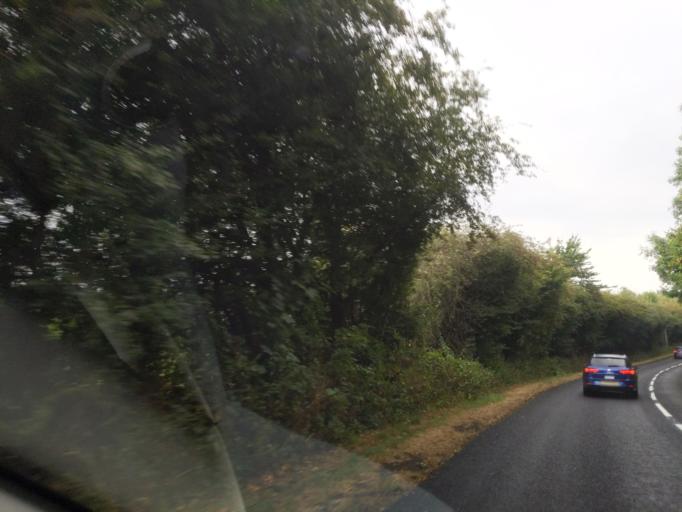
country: GB
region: England
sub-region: Devon
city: Plympton
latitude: 50.3684
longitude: -4.0669
